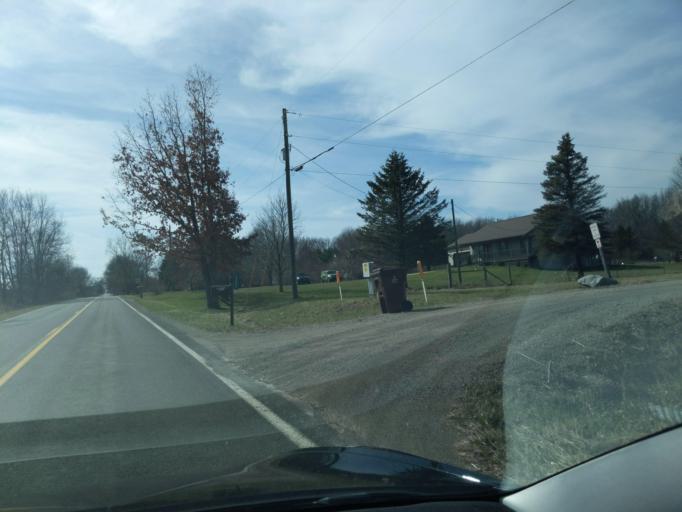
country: US
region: Michigan
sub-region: Ingham County
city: Stockbridge
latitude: 42.4831
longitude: -84.2249
